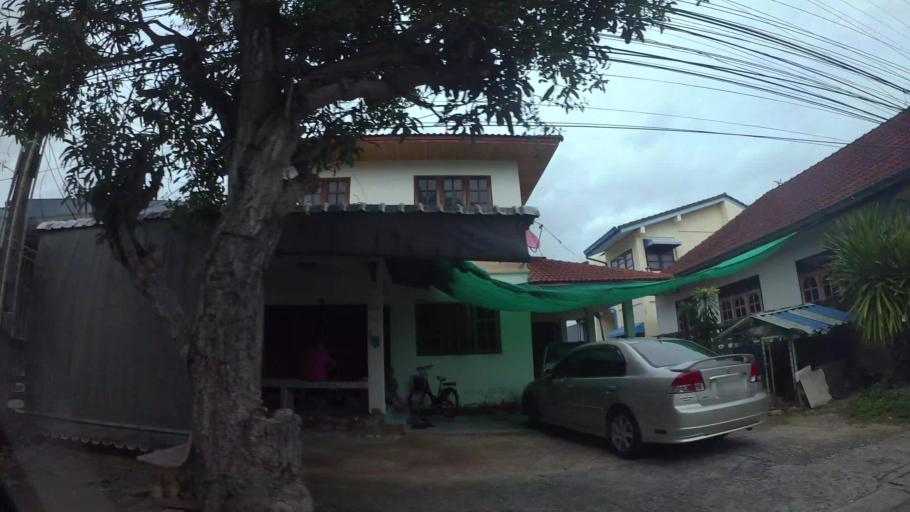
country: TH
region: Rayong
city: Rayong
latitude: 12.6712
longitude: 101.2791
